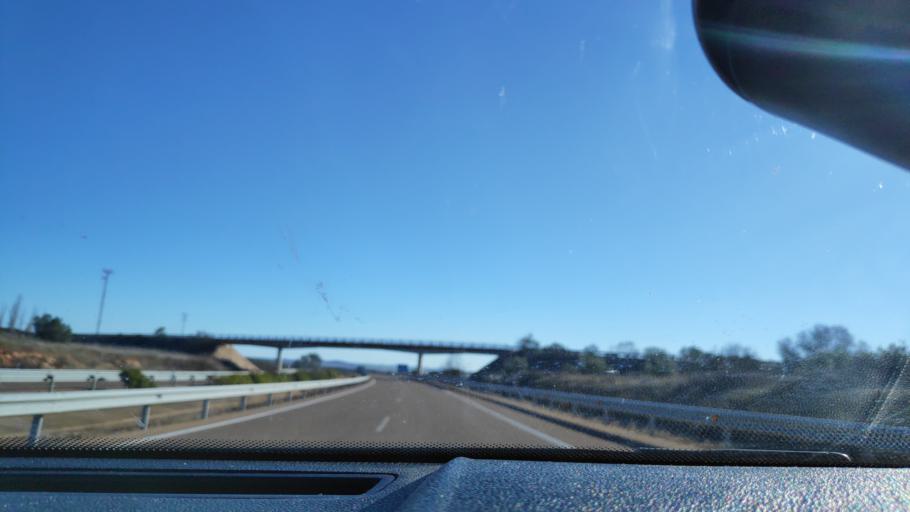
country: ES
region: Extremadura
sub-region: Provincia de Badajoz
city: Puebla de Sancho Perez
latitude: 38.3857
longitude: -6.3399
